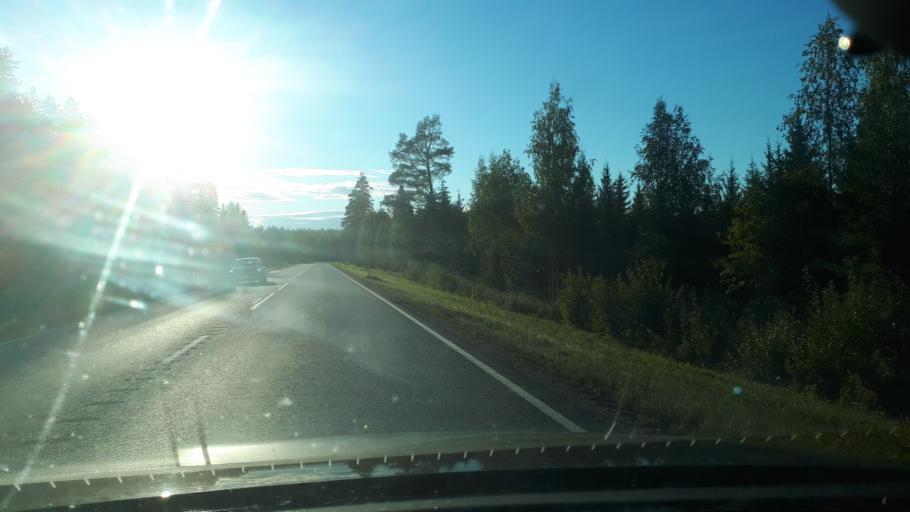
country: FI
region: Northern Savo
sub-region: Ylae-Savo
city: Iisalmi
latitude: 63.6432
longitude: 27.1195
